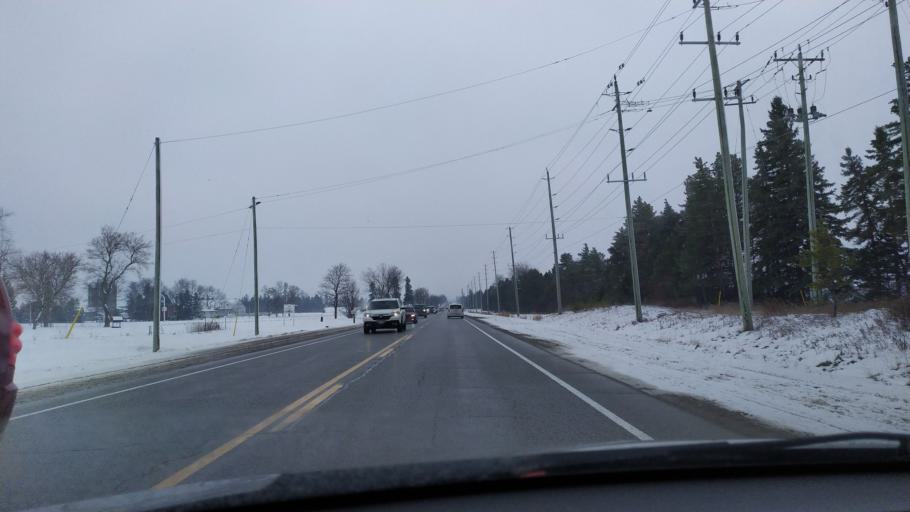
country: CA
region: Ontario
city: Waterloo
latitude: 43.6182
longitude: -80.6807
